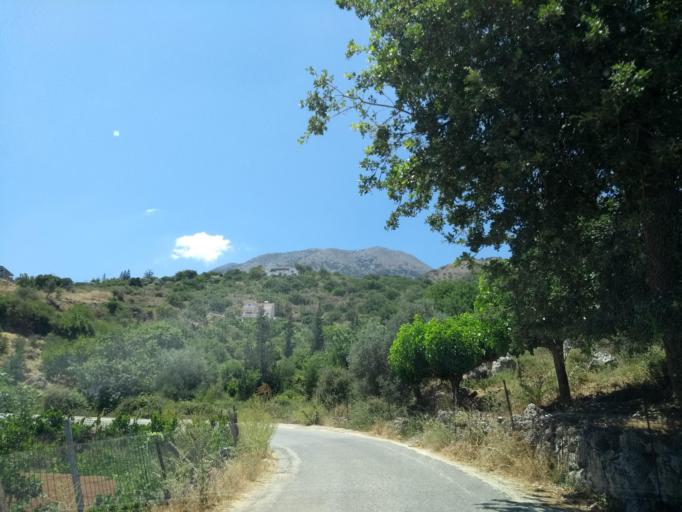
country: GR
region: Crete
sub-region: Nomos Chanias
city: Georgioupolis
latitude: 35.3184
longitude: 24.2891
